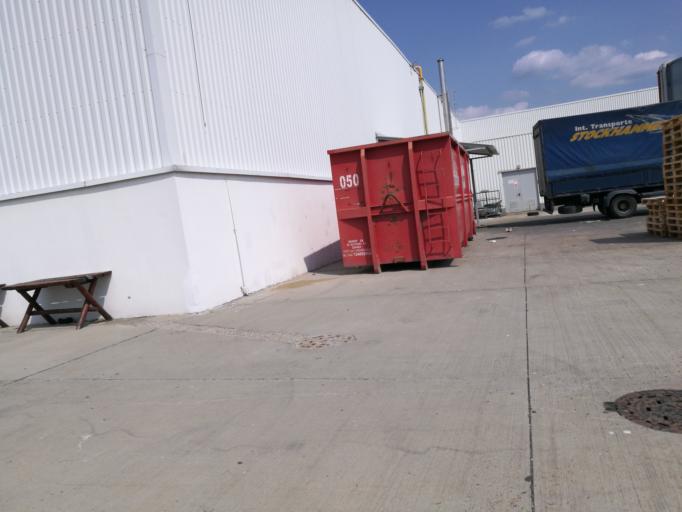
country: RO
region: Iasi
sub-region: Comuna Miroslava
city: Miroslava
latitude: 47.1664
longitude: 27.5117
